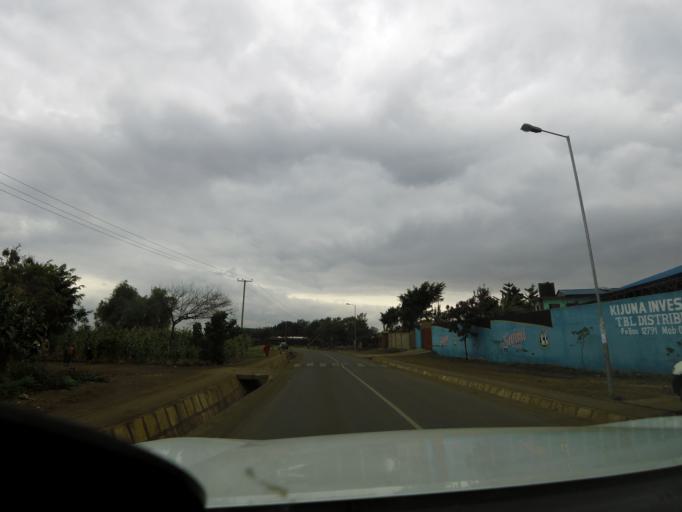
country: TZ
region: Arusha
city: Arusha
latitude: -3.3645
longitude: 36.6607
